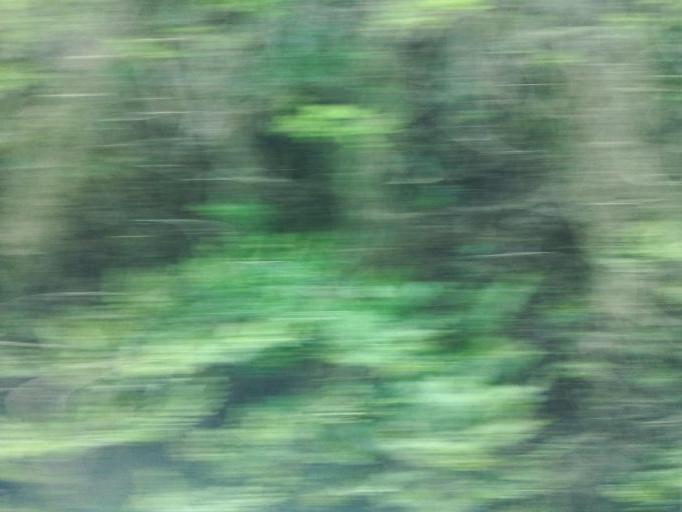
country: BR
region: Minas Gerais
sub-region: Timoteo
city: Timoteo
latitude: -19.5630
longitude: -42.7152
